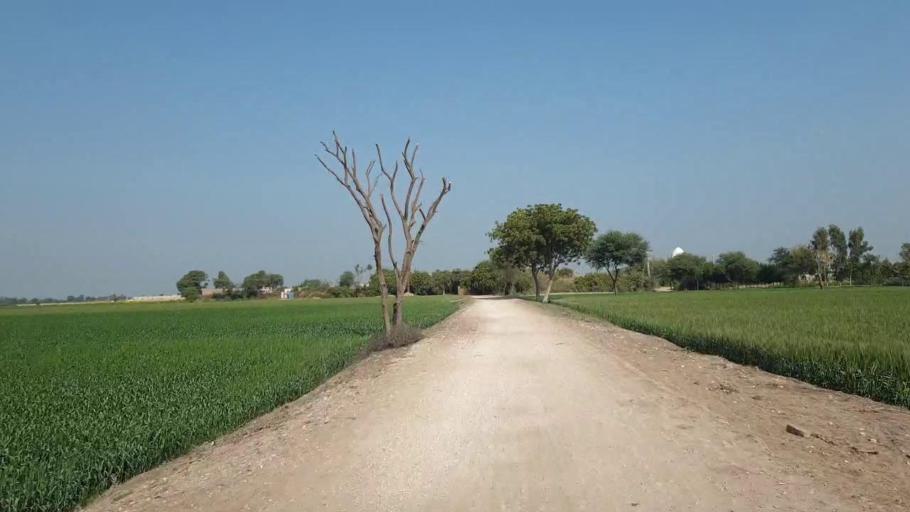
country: PK
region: Sindh
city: Hala
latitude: 25.9298
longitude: 68.4046
